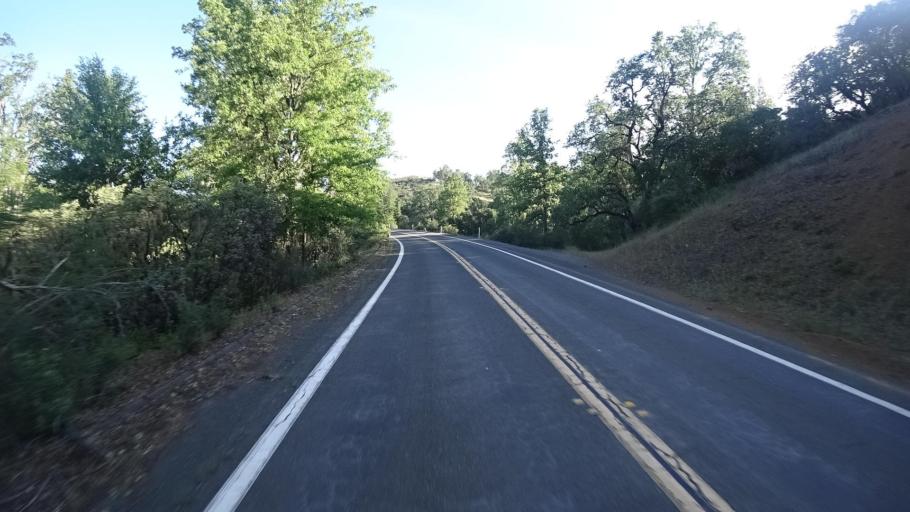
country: US
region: California
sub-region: Lake County
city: North Lakeport
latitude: 39.1015
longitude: -122.9686
